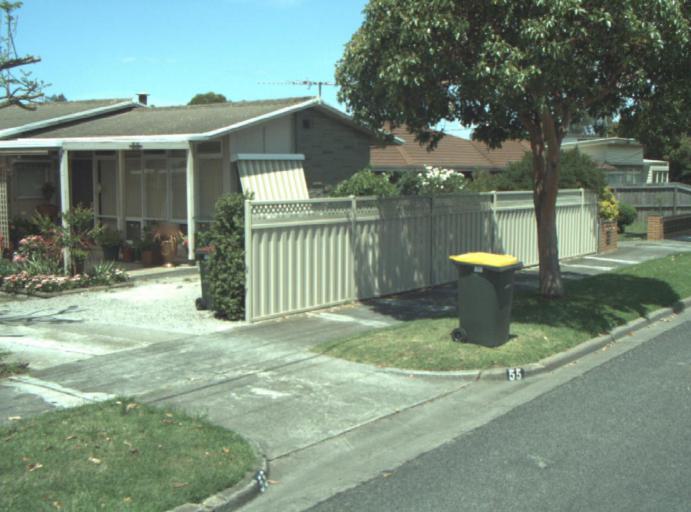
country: AU
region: Victoria
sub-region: Greater Geelong
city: Hamlyn Heights
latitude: -38.1325
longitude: 144.3194
